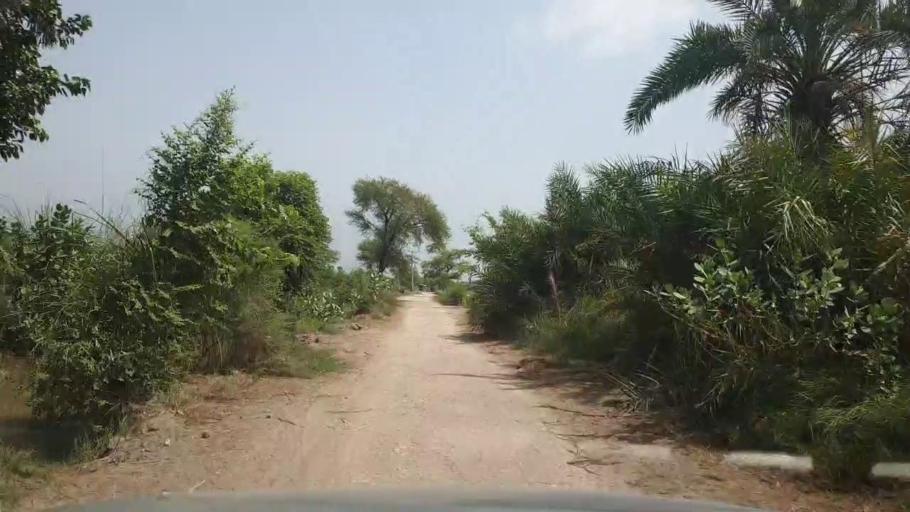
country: PK
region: Sindh
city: Garhi Yasin
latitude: 27.9447
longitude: 68.3739
